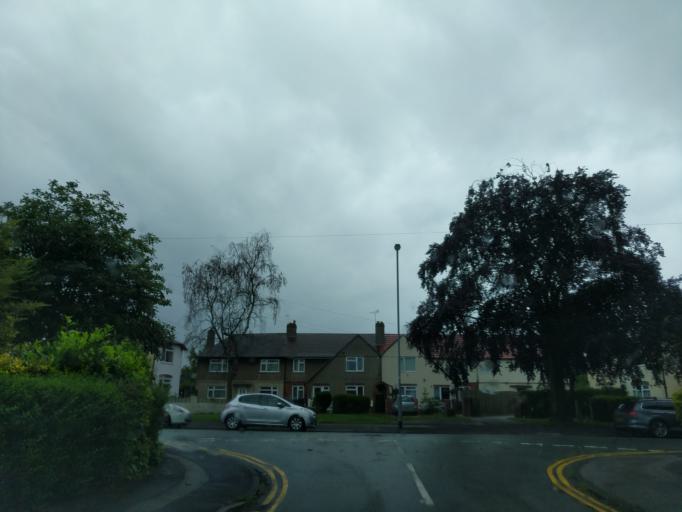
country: GB
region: England
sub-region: Staffordshire
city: Stafford
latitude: 52.8052
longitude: -2.1034
